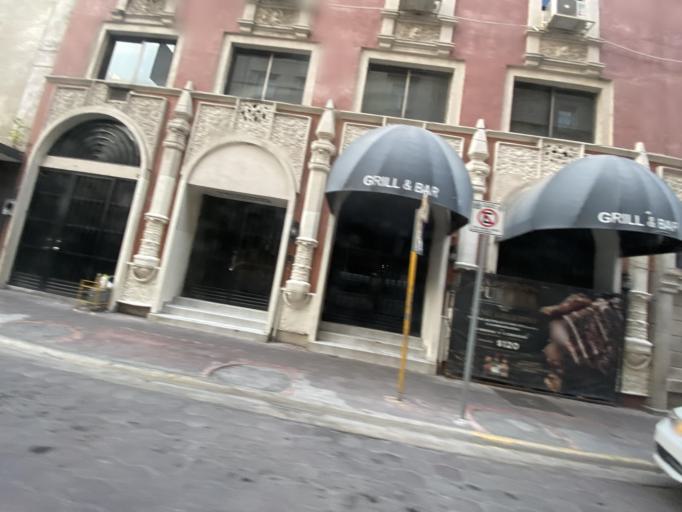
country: MX
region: Nuevo Leon
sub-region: Monterrey
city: Monterrey
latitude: 25.6663
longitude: -100.3124
